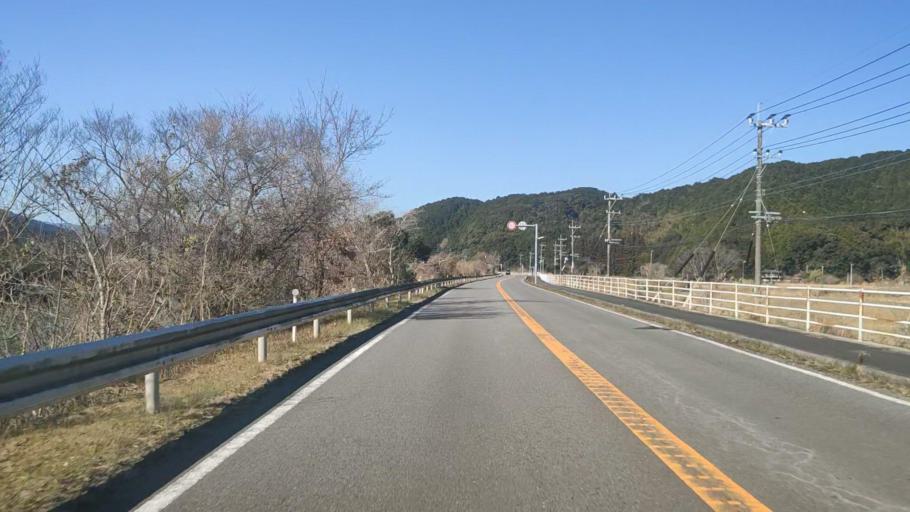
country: JP
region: Oita
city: Saiki
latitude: 32.9375
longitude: 131.9164
